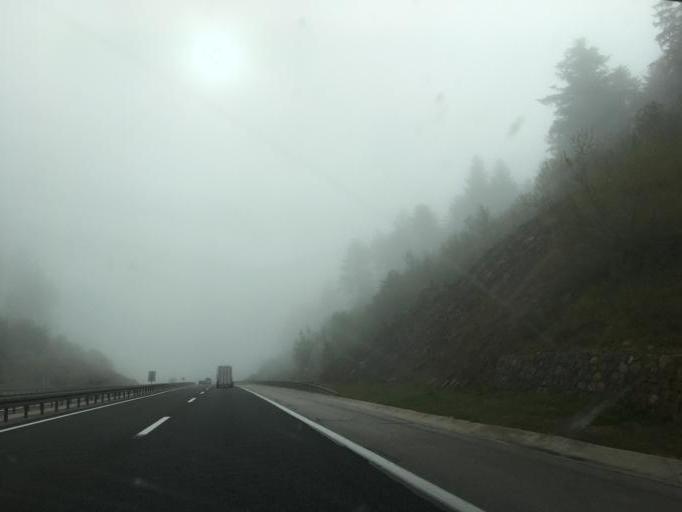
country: HR
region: Licko-Senjska
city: Otocac
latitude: 44.8496
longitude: 15.2317
